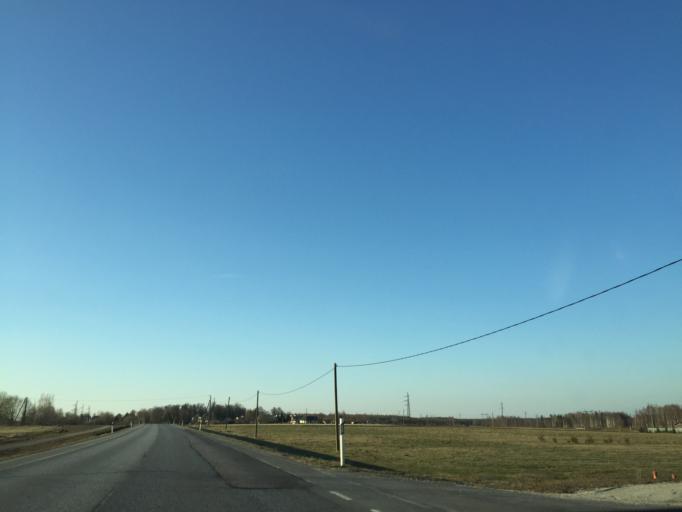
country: EE
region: Ida-Virumaa
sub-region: Johvi vald
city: Johvi
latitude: 59.2639
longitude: 27.5146
